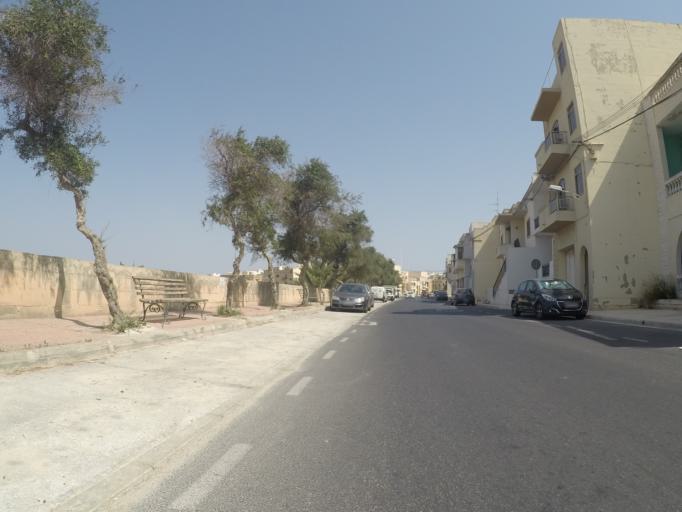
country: MT
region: Ir-Rabat
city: Rabat
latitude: 35.8764
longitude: 14.3956
